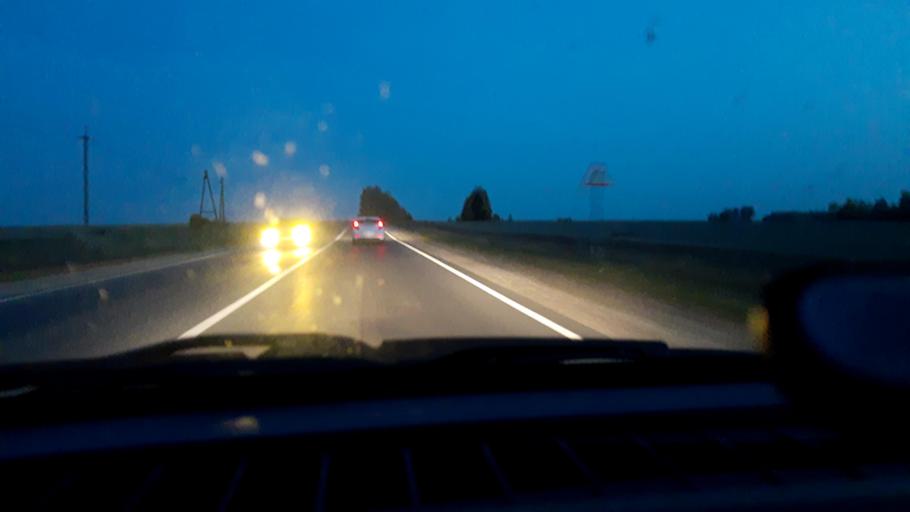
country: RU
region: Nizjnij Novgorod
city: Gorodets
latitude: 56.6287
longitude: 43.5415
